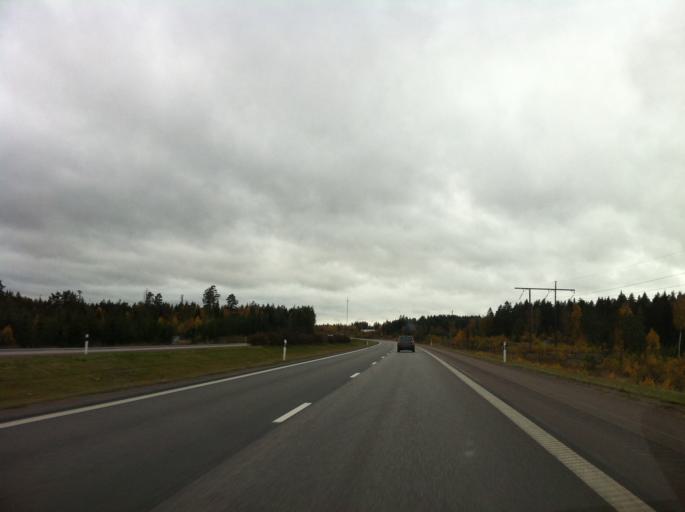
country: SE
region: OEstergoetland
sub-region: Vadstena Kommun
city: Herrestad
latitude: 58.2909
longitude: 14.8929
